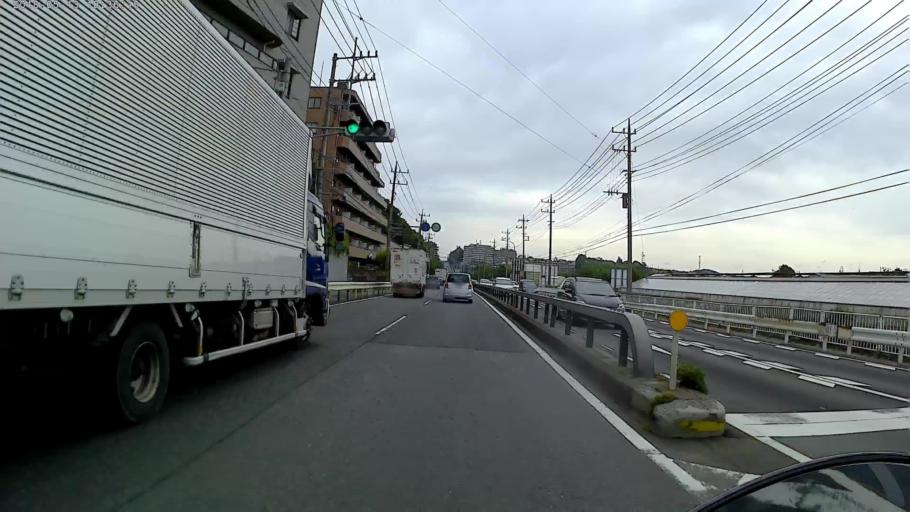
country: JP
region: Tokyo
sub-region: Machida-shi
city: Machida
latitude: 35.5320
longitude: 139.5045
